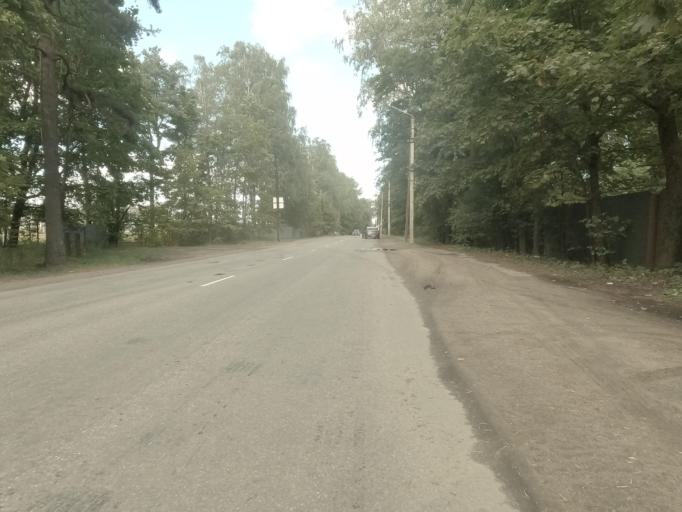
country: RU
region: Leningrad
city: Vsevolozhsk
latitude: 60.0163
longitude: 30.6744
